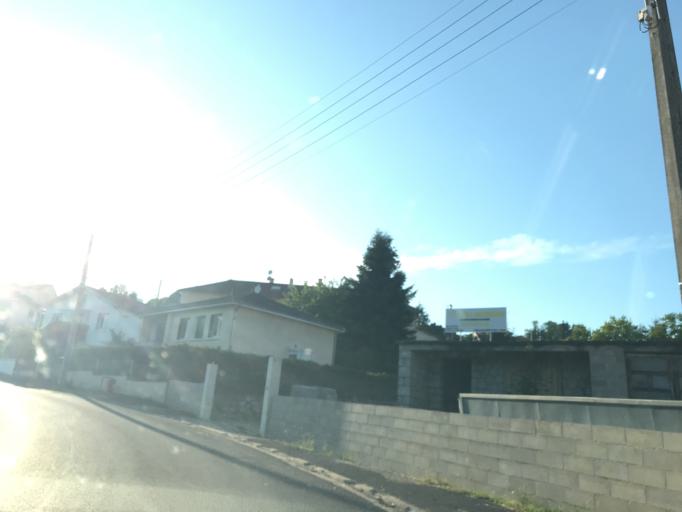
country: FR
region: Auvergne
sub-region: Departement du Puy-de-Dome
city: Saint-Remy-sur-Durolle
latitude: 45.8893
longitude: 3.5970
